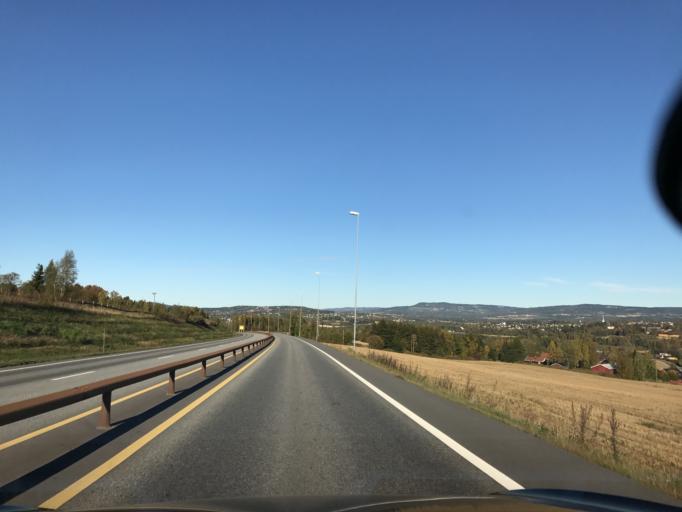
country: NO
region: Hedmark
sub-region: Stange
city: Stange
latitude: 60.7779
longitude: 11.1483
